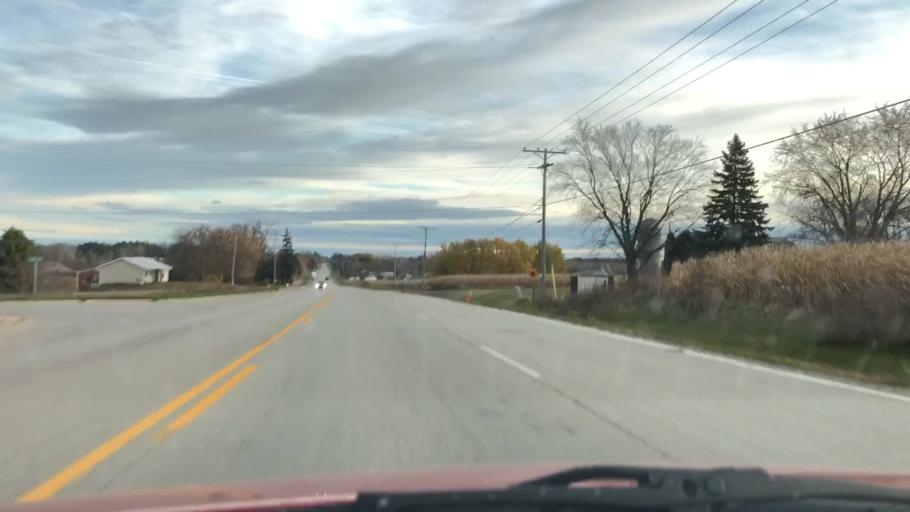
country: US
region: Wisconsin
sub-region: Brown County
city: Oneida
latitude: 44.4335
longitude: -88.2360
